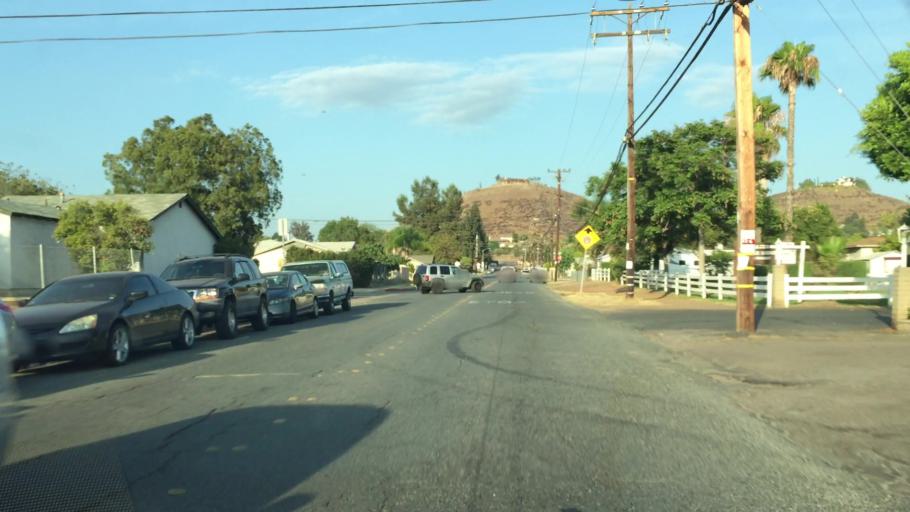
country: US
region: California
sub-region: San Diego County
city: Bostonia
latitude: 32.8191
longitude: -116.9511
